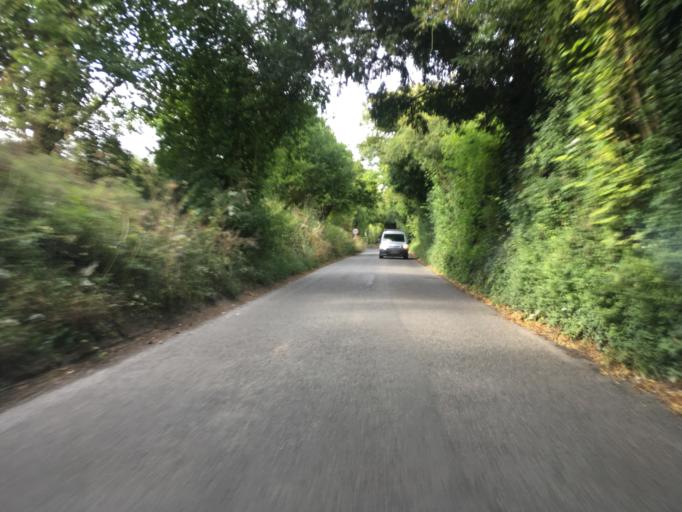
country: GB
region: England
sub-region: Hampshire
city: Colden Common
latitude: 51.0020
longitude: -1.2714
